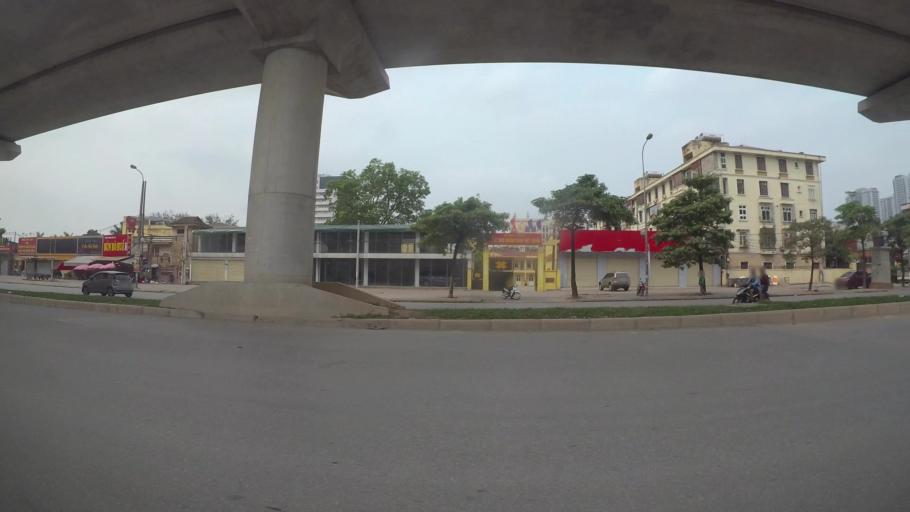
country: VN
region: Ha Noi
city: Cau Dien
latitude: 21.0420
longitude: 105.7601
